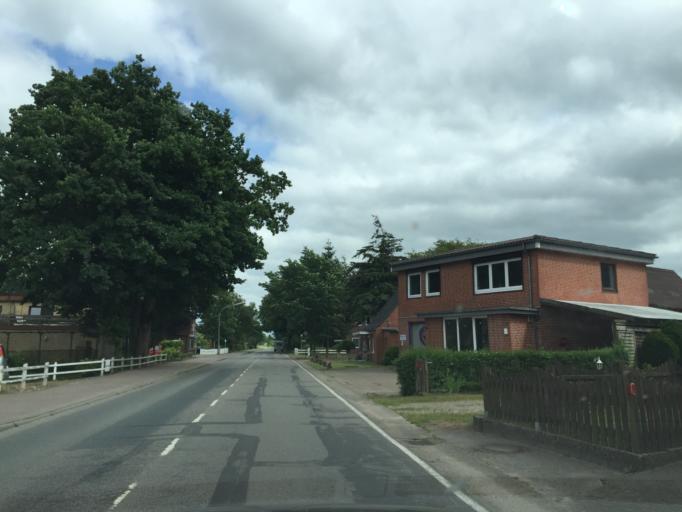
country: DE
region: Schleswig-Holstein
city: Humptrup
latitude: 54.8704
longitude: 8.8916
